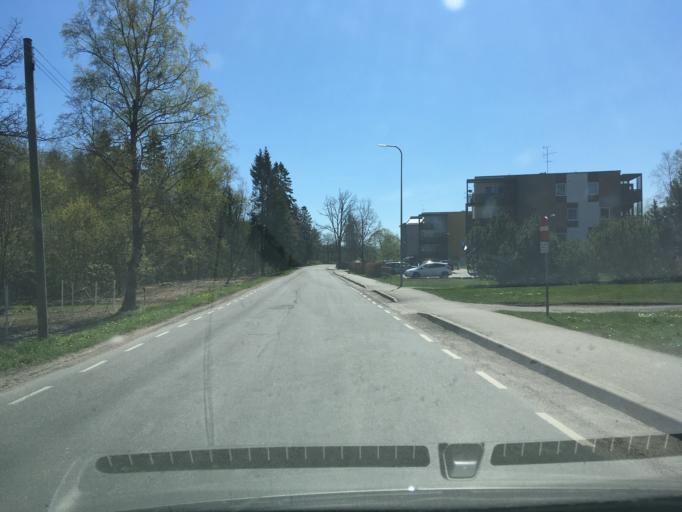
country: EE
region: Harju
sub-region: Raasiku vald
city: Arukula
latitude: 59.3658
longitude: 25.0819
